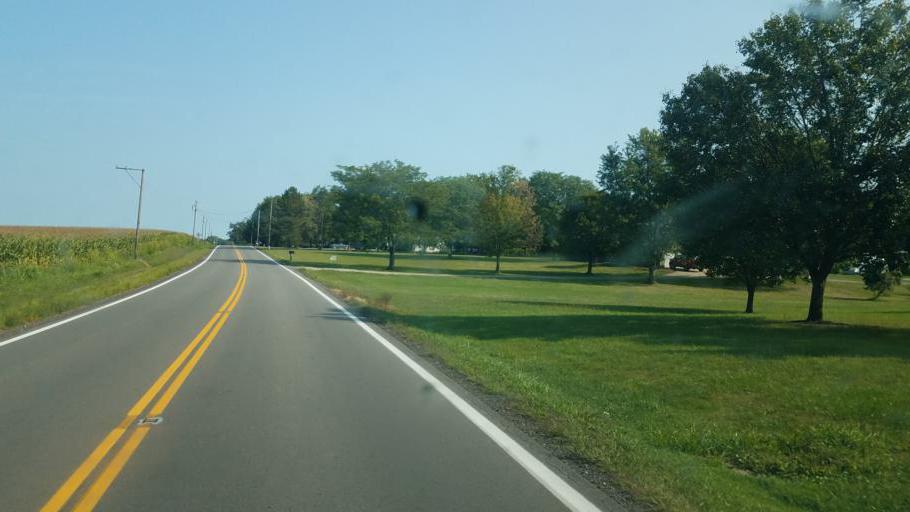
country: US
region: Ohio
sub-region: Richland County
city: Shelby
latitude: 40.8315
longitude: -82.6553
